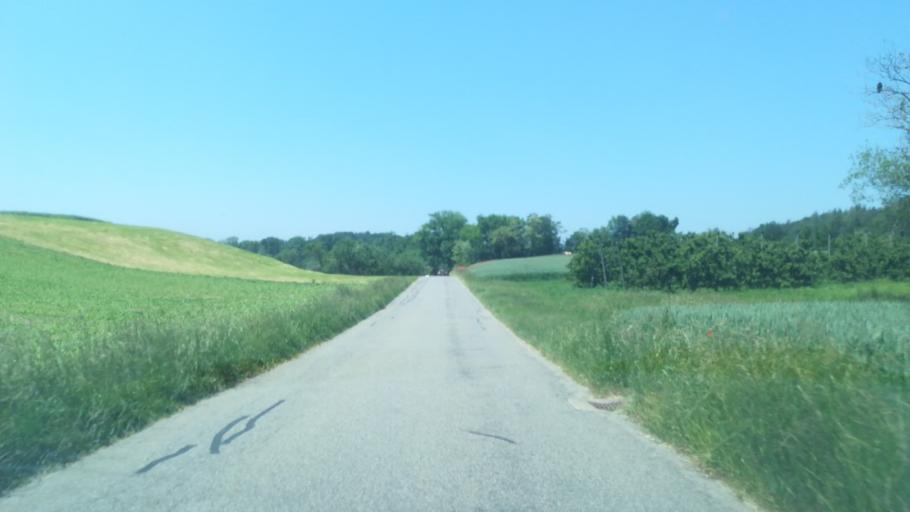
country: CH
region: Thurgau
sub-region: Frauenfeld District
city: Pfyn
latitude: 47.6278
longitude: 8.9288
